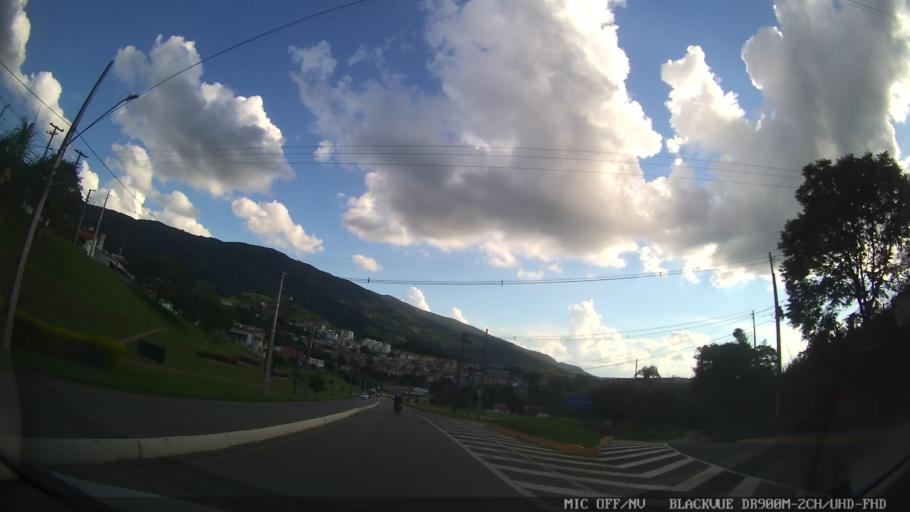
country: BR
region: Minas Gerais
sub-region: Extrema
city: Extrema
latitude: -22.8590
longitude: -46.3299
